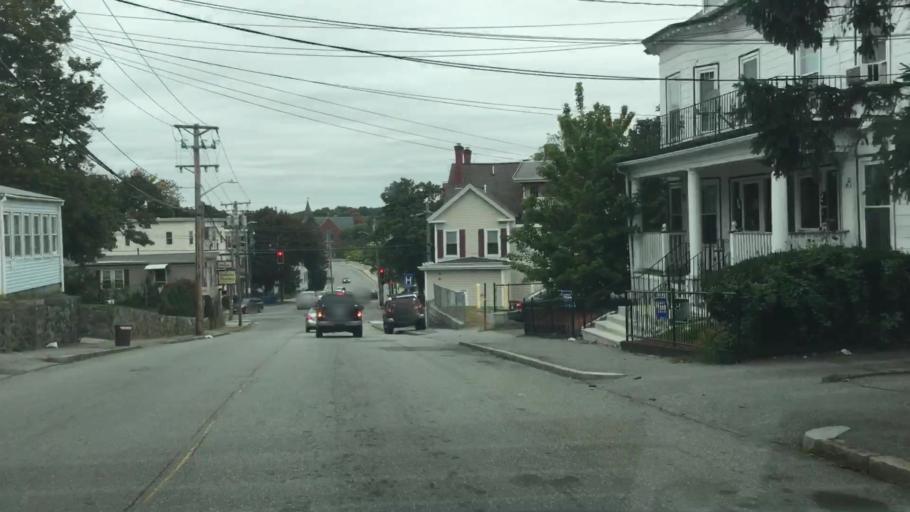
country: US
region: Massachusetts
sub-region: Middlesex County
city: Lowell
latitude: 42.6477
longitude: -71.3280
